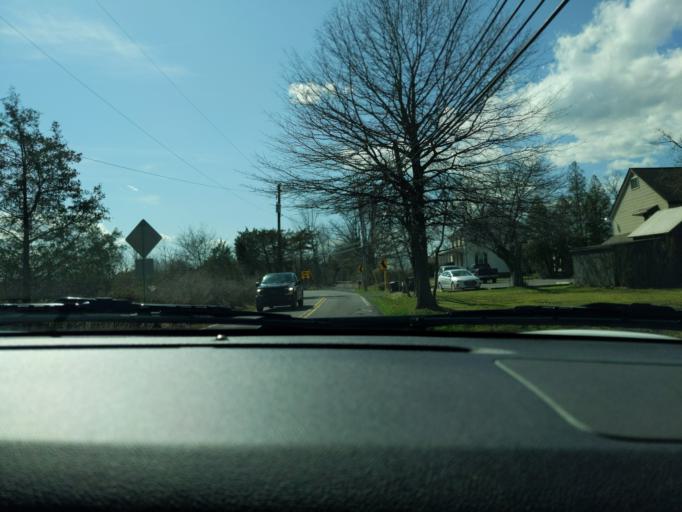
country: US
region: Pennsylvania
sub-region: Bucks County
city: Richlandtown
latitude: 40.4539
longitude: -75.3025
